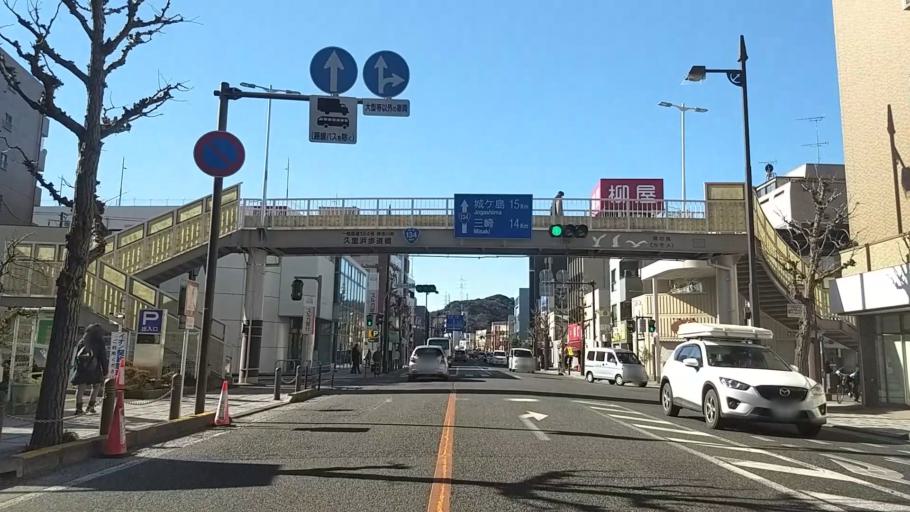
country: JP
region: Kanagawa
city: Yokosuka
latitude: 35.2305
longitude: 139.7046
